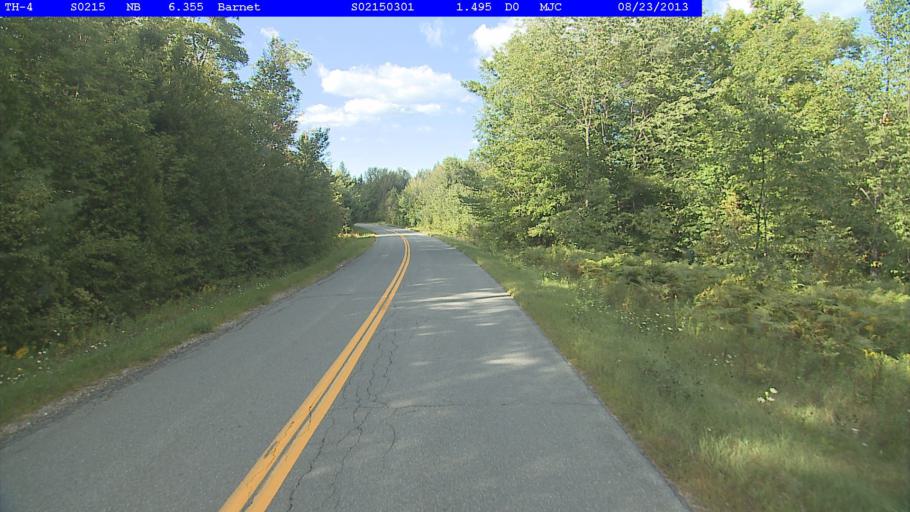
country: US
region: New Hampshire
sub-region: Grafton County
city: Woodsville
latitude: 44.2935
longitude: -72.1628
